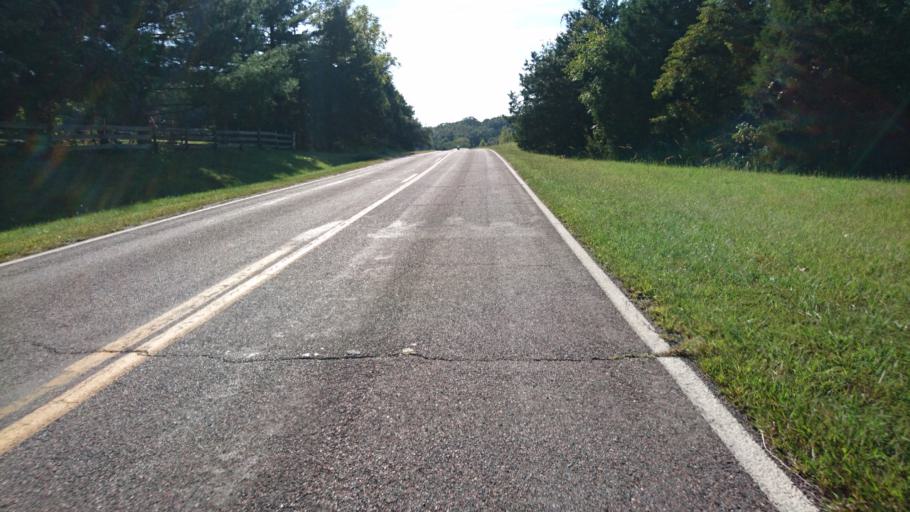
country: US
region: Missouri
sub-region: Crawford County
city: Bourbon
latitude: 38.1305
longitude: -91.3002
